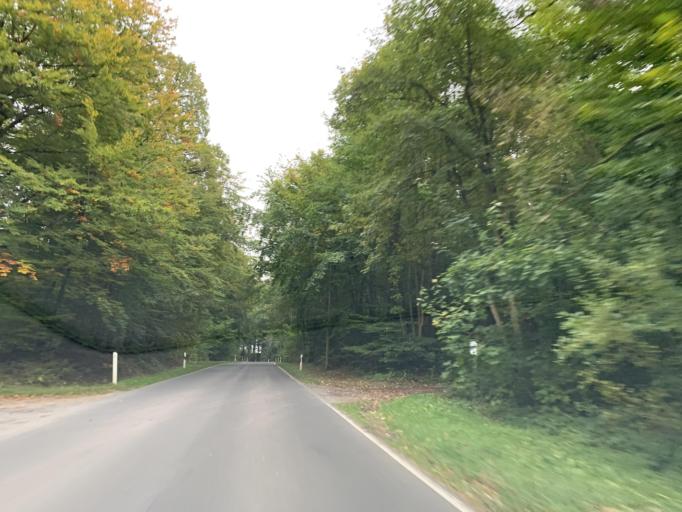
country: DE
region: Mecklenburg-Vorpommern
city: Burg Stargard
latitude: 53.4763
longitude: 13.2893
